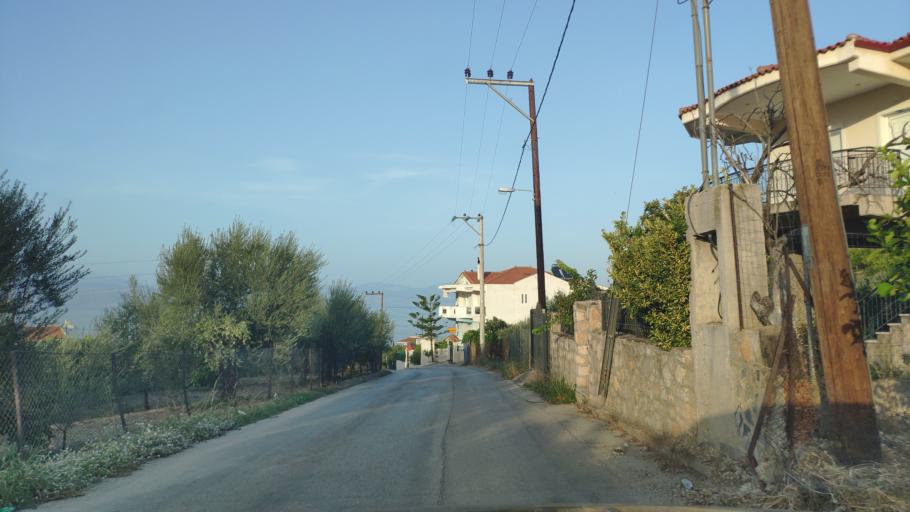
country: GR
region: West Greece
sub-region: Nomos Achaias
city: Aiyira
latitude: 38.1287
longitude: 22.4008
